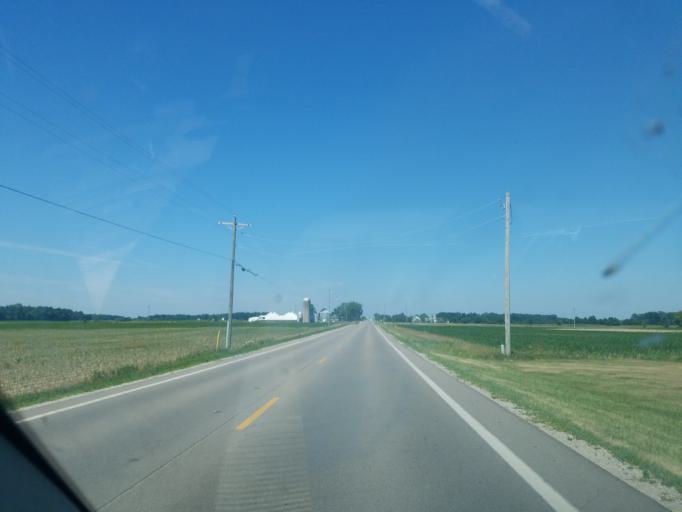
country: US
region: Ohio
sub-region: Shelby County
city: Botkins
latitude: 40.4388
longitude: -84.1418
